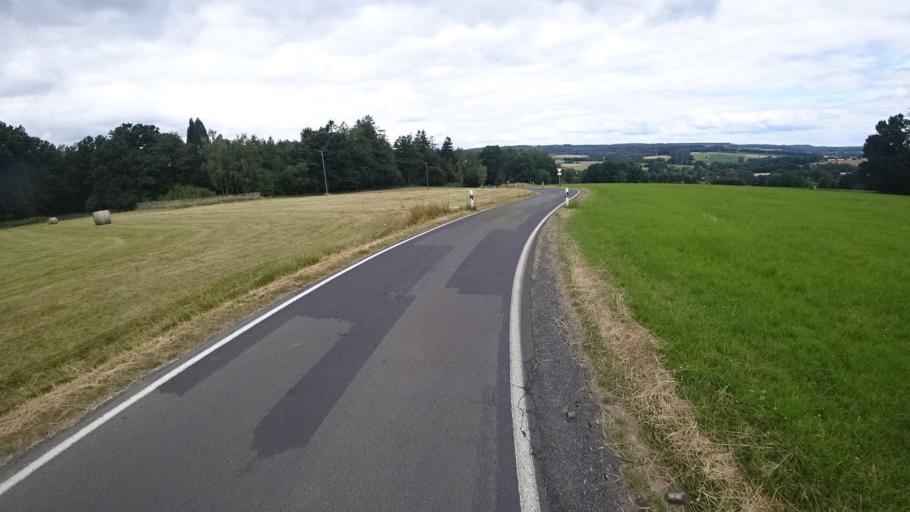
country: DE
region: Rheinland-Pfalz
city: Seifen
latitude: 50.6813
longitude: 7.5246
